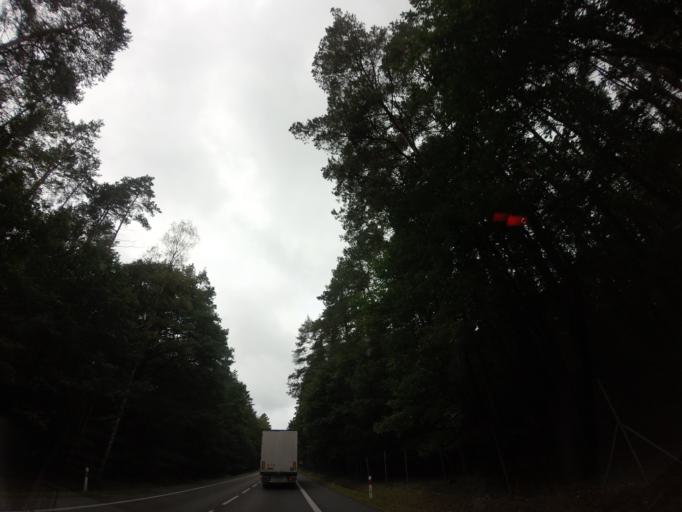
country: PL
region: West Pomeranian Voivodeship
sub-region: Powiat kamienski
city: Miedzyzdroje
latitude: 53.8913
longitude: 14.4914
